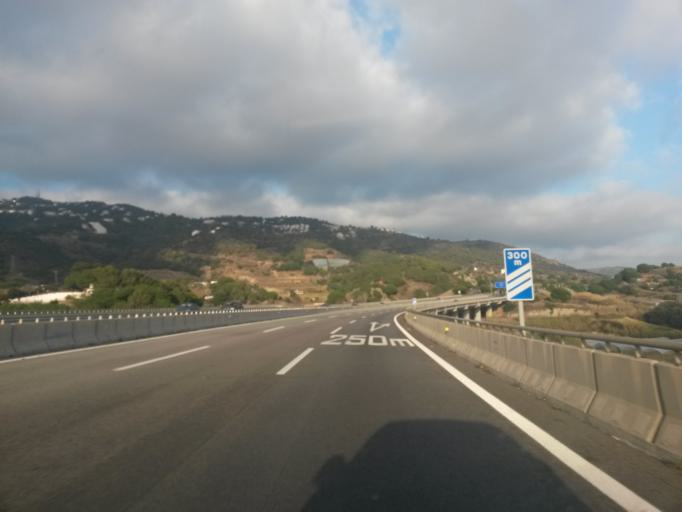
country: ES
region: Catalonia
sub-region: Provincia de Barcelona
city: Calella
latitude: 41.6234
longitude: 2.6485
